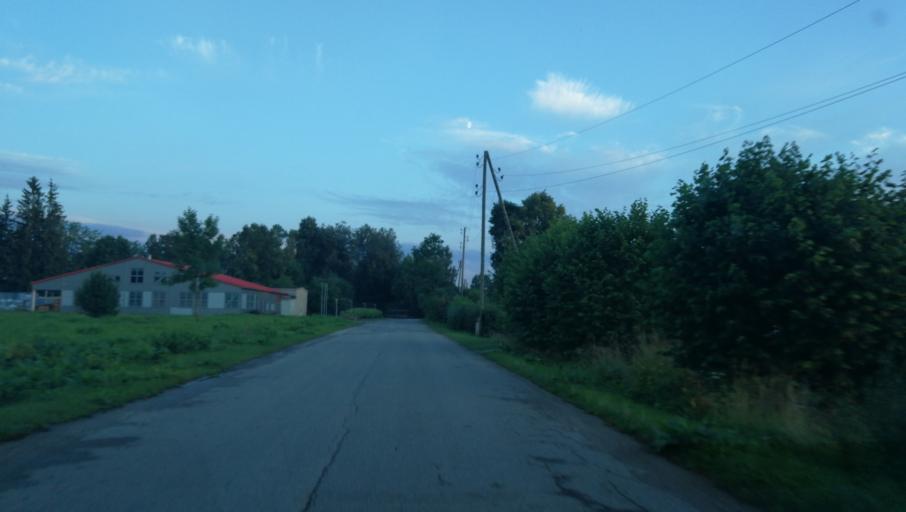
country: LV
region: Cesu Rajons
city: Cesis
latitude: 57.3163
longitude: 25.3018
